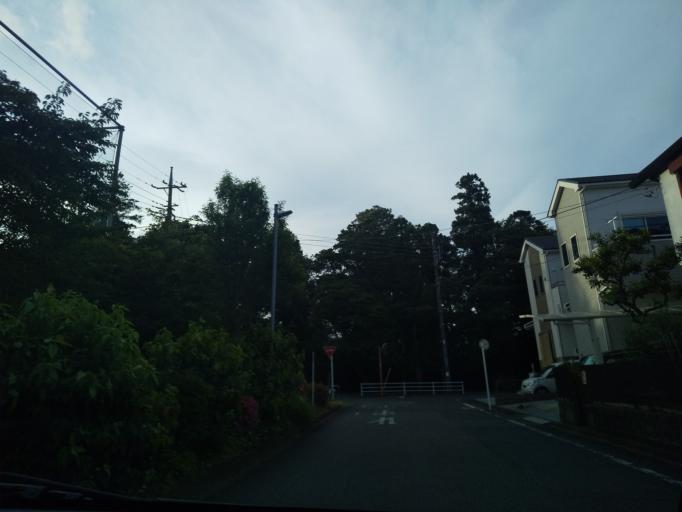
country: JP
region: Kanagawa
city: Zama
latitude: 35.5430
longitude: 139.3907
